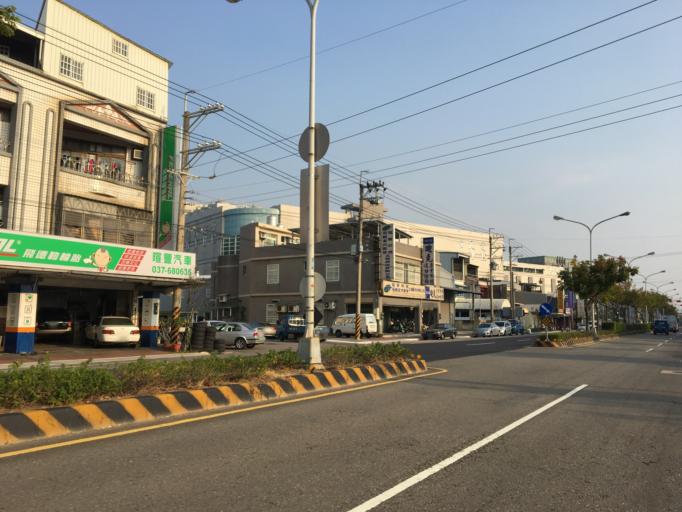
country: TW
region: Taiwan
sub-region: Hsinchu
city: Hsinchu
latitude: 24.7122
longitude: 120.9228
